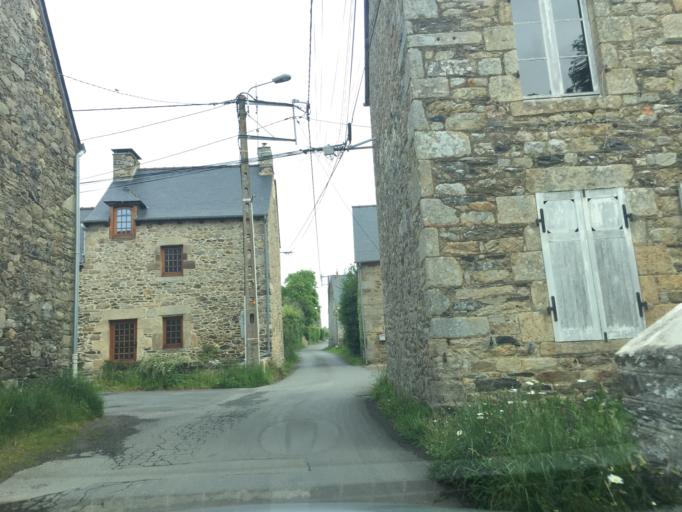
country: FR
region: Brittany
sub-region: Departement des Cotes-d'Armor
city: Saint-Cast-le-Guildo
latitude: 48.5954
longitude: -2.2341
